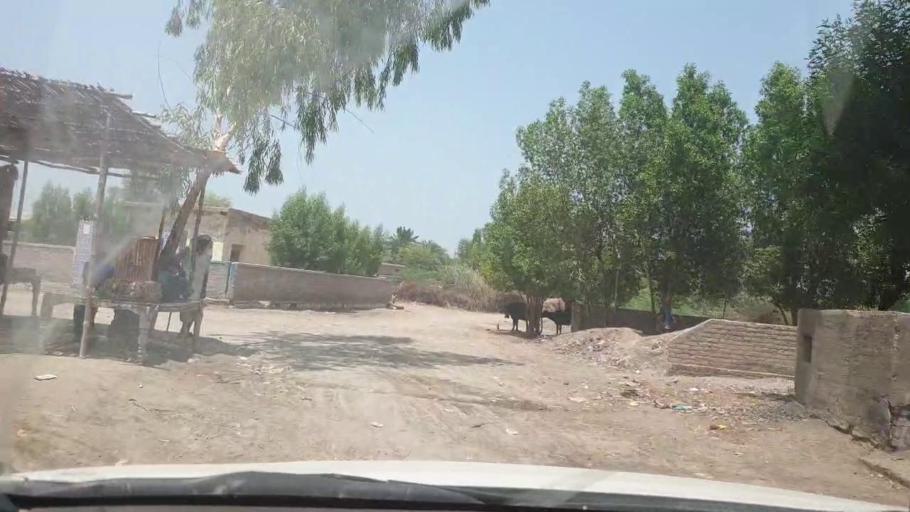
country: PK
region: Sindh
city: Lakhi
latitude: 27.8722
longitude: 68.6905
